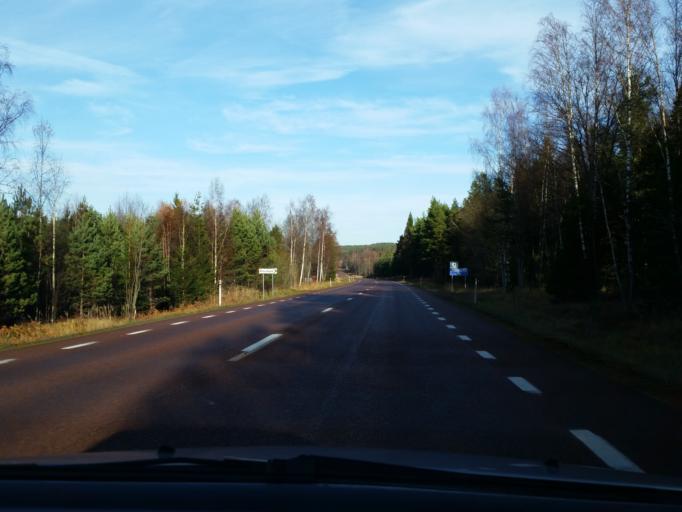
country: AX
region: Alands landsbygd
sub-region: Finstroem
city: Finstroem
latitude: 60.2917
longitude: 19.9534
